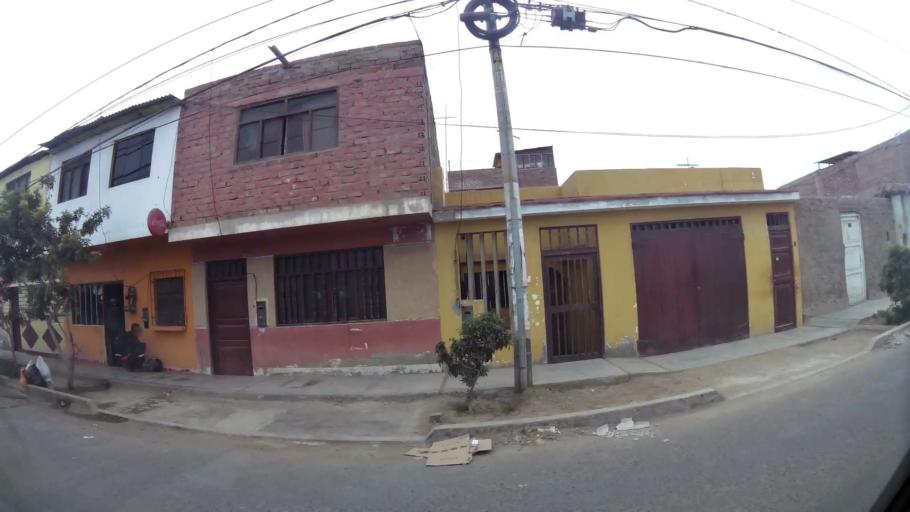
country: PE
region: La Libertad
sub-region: Provincia de Trujillo
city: Buenos Aires
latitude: -8.1415
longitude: -79.0567
